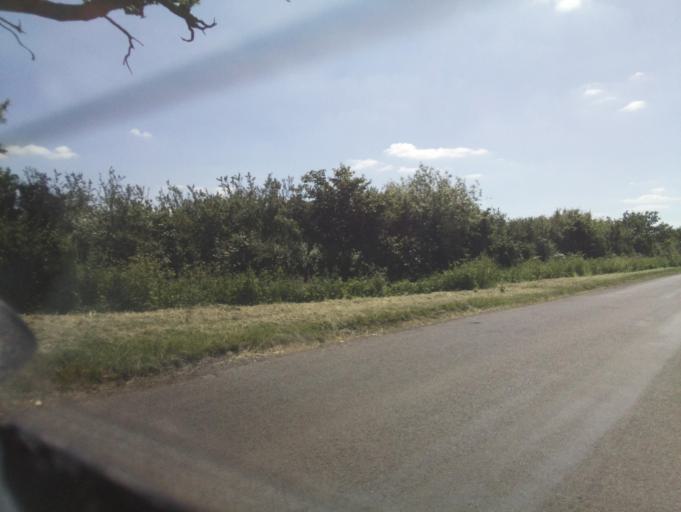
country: GB
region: England
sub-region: Wiltshire
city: Lyneham
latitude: 51.4859
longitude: -1.9411
